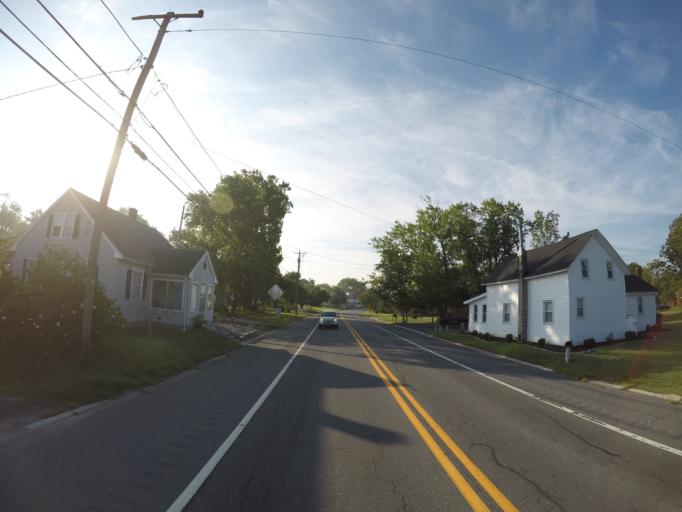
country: US
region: Delaware
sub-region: Sussex County
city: Selbyville
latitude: 38.4952
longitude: -75.1689
